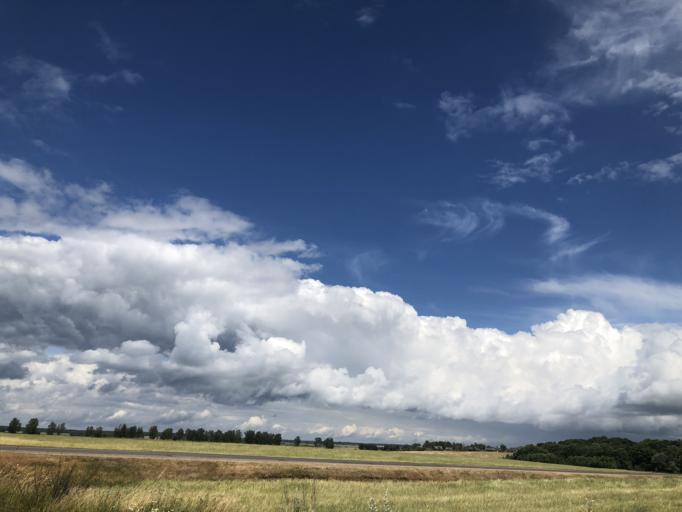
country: BY
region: Minsk
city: Kapyl'
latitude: 53.2567
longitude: 26.9424
